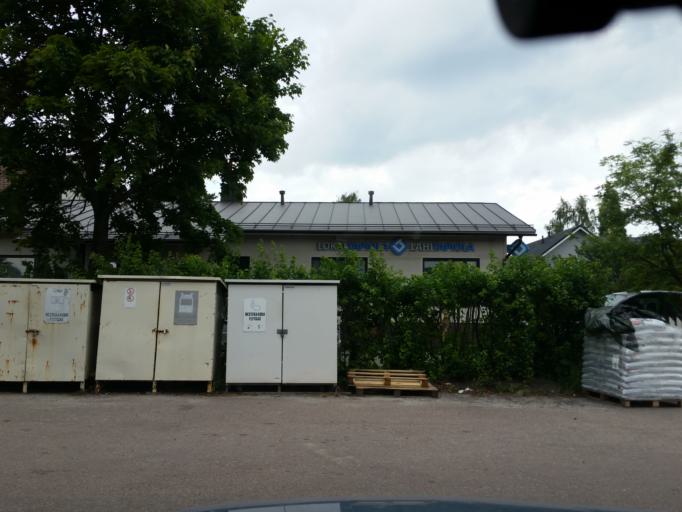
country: FI
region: Varsinais-Suomi
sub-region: Aboland-Turunmaa
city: Nagu
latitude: 60.1929
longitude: 21.9102
